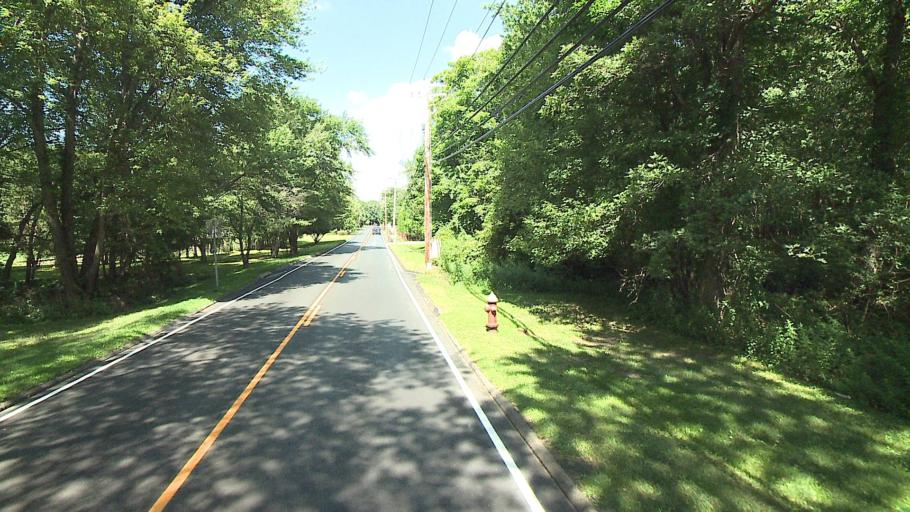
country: US
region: Connecticut
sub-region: Fairfield County
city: Shelton
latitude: 41.2911
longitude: -73.1498
